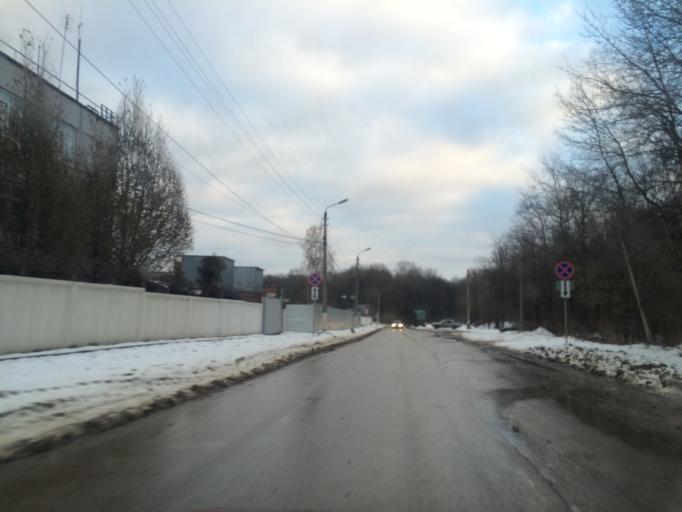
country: RU
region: Tula
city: Tula
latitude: 54.2167
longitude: 37.7126
